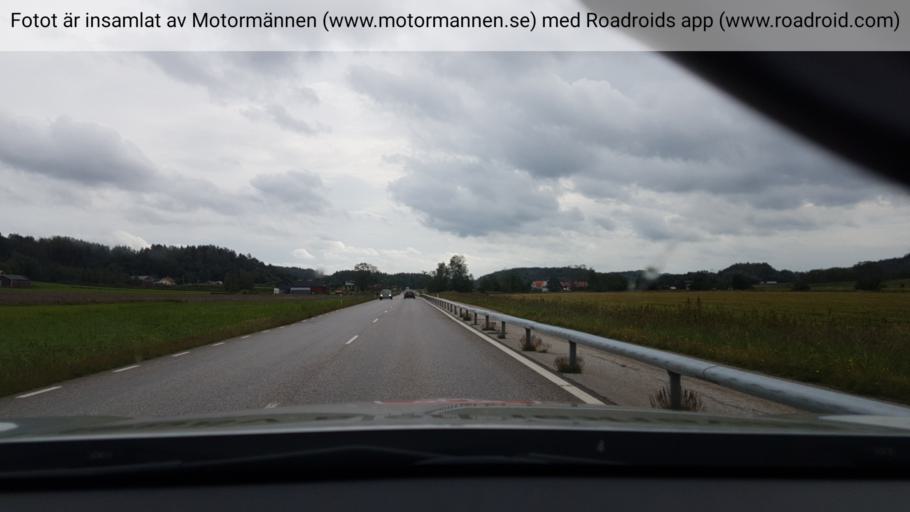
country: SE
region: Vaestra Goetaland
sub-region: Munkedals Kommun
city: Munkedal
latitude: 58.5140
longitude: 11.5756
